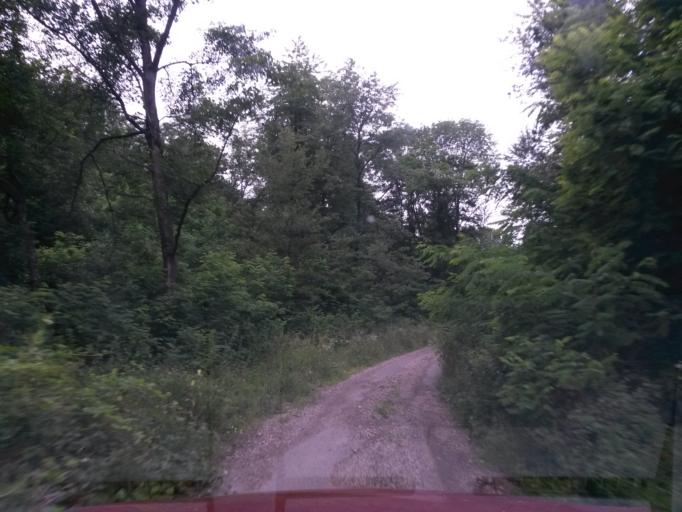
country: SK
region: Banskobystricky
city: Velky Krtis
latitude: 48.3066
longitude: 19.4128
